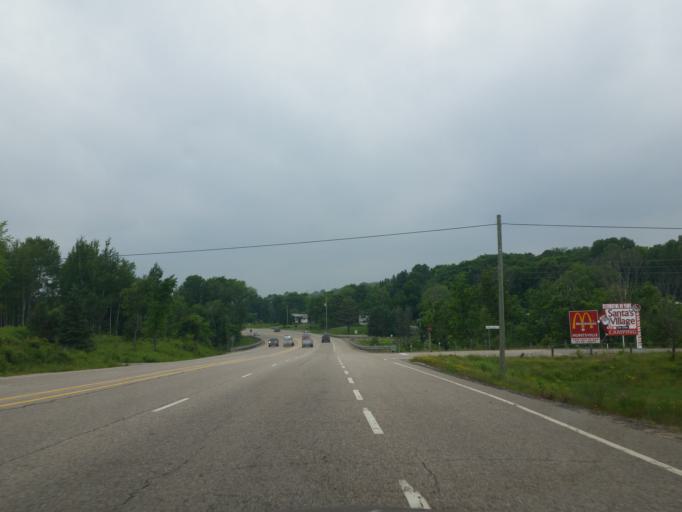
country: CA
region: Ontario
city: Huntsville
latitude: 45.3418
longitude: -79.1728
